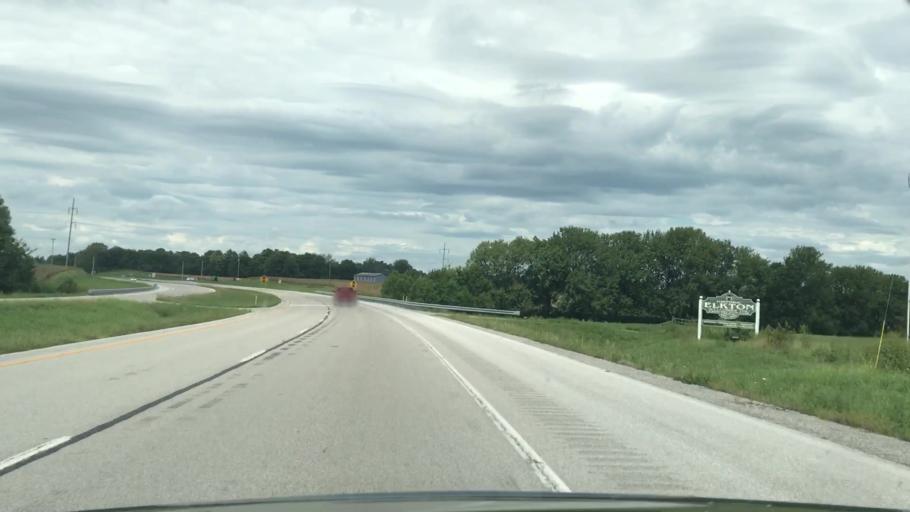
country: US
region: Kentucky
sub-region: Todd County
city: Elkton
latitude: 36.8227
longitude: -87.1468
